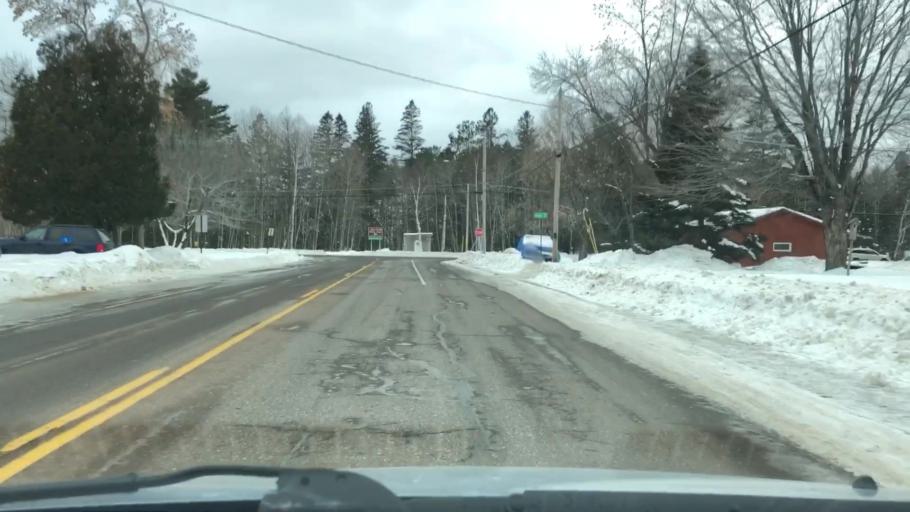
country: US
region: Minnesota
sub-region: Carlton County
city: Carlton
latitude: 46.6636
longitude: -92.3981
